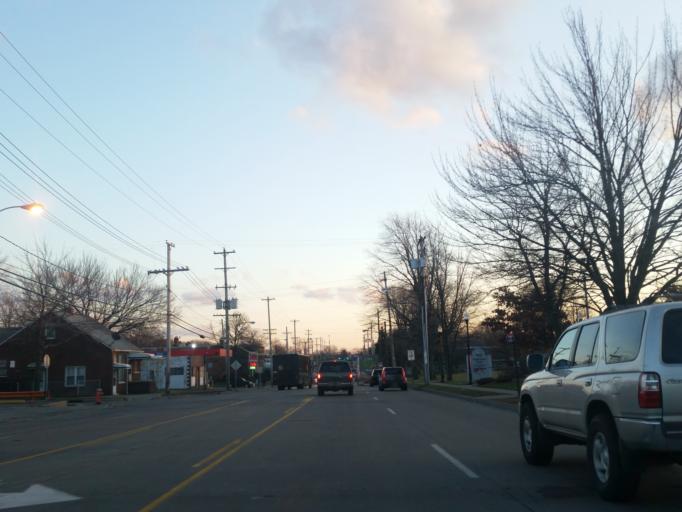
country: US
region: Ohio
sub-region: Cuyahoga County
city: Brooklyn
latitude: 41.4560
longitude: -81.7691
